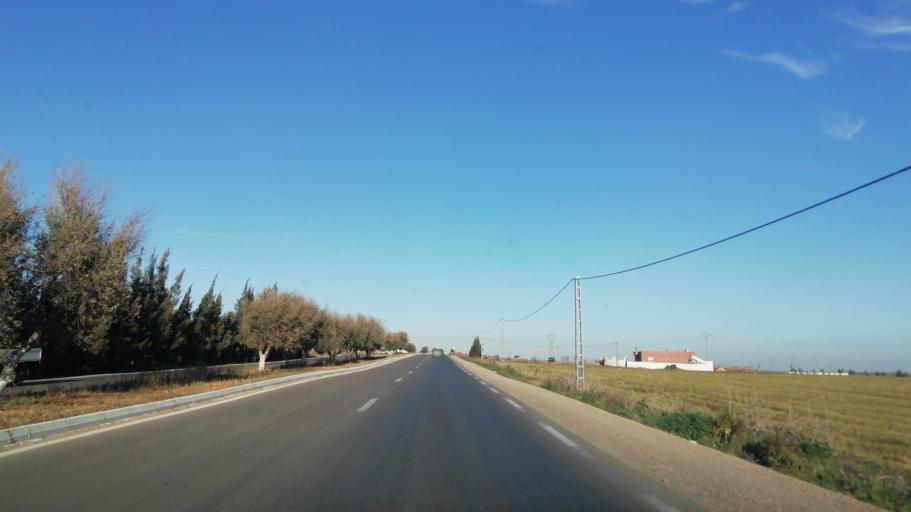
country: DZ
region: Mascara
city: Bou Hanifia el Hamamat
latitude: 35.3404
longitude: 0.0487
